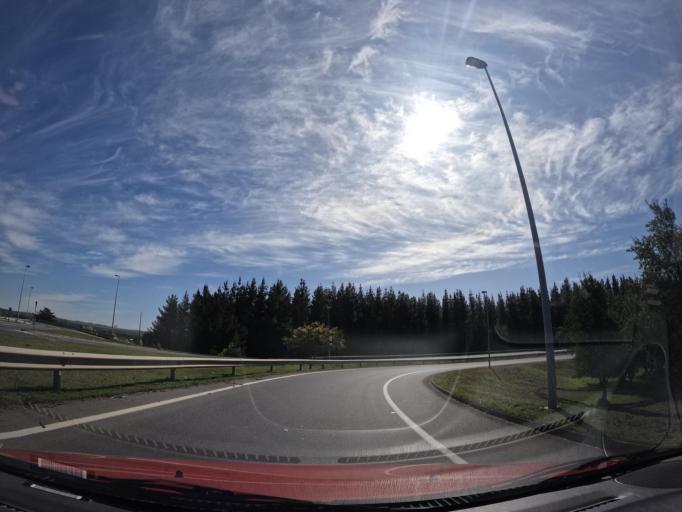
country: CL
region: Biobio
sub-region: Provincia de Biobio
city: Cabrero
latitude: -36.9324
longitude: -72.3502
